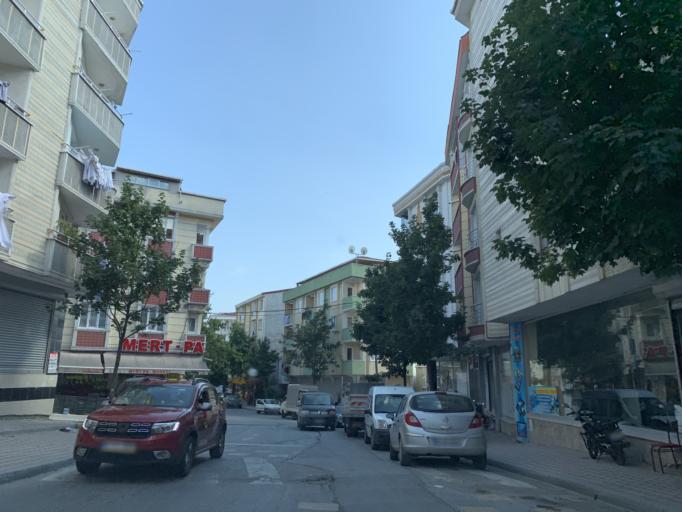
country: TR
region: Istanbul
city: Esenyurt
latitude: 41.0378
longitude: 28.6752
